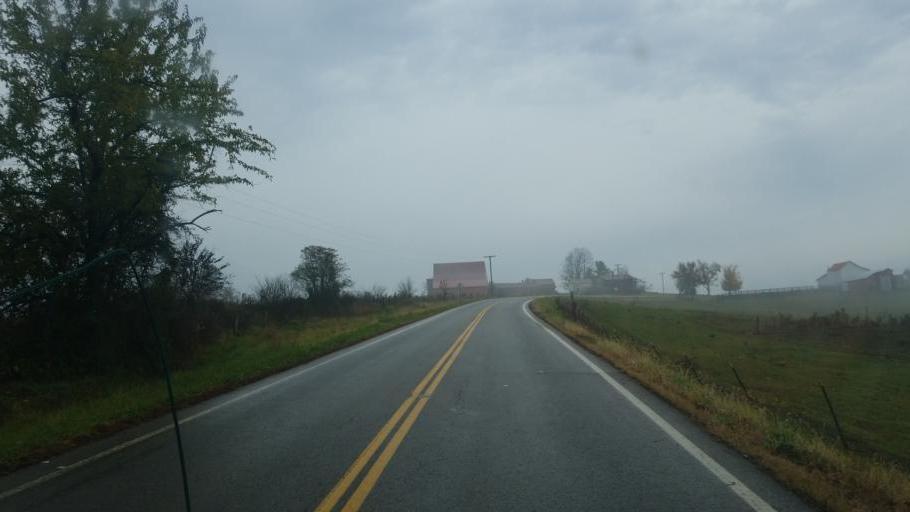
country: US
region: Ohio
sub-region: Morgan County
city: McConnelsville
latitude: 39.4749
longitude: -81.8776
